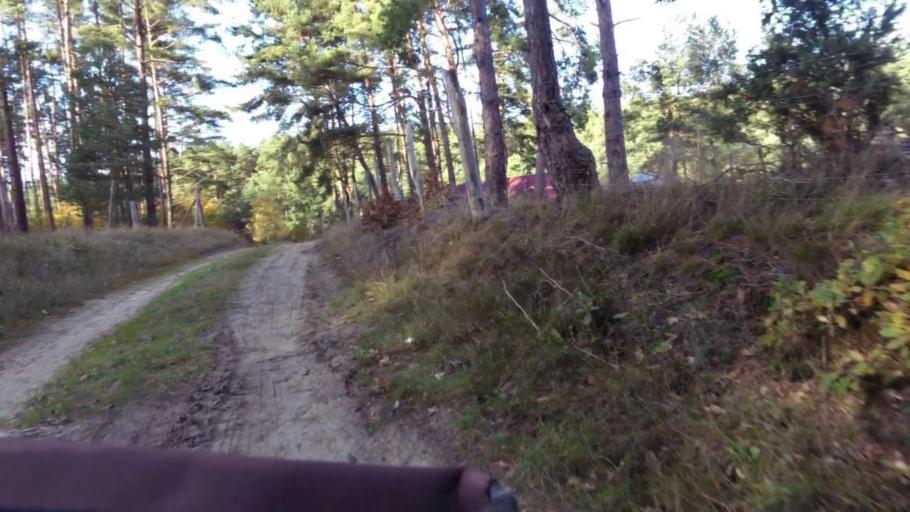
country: PL
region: West Pomeranian Voivodeship
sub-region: Powiat kamienski
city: Wolin
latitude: 53.8690
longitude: 14.5268
